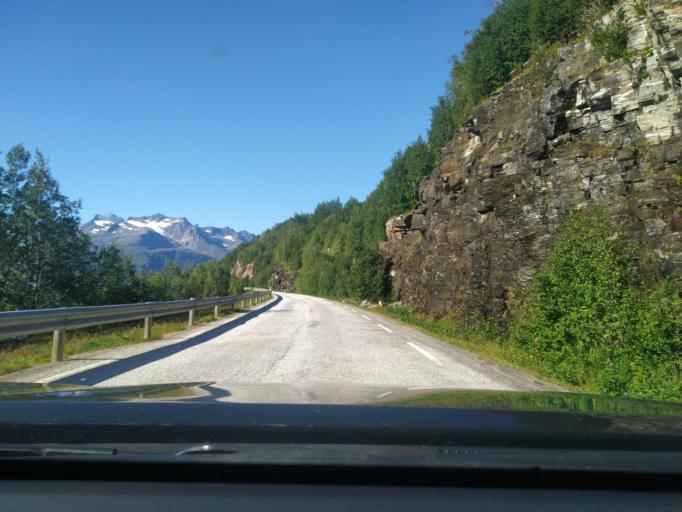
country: NO
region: Troms
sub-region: Dyroy
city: Brostadbotn
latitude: 68.9196
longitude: 17.6060
